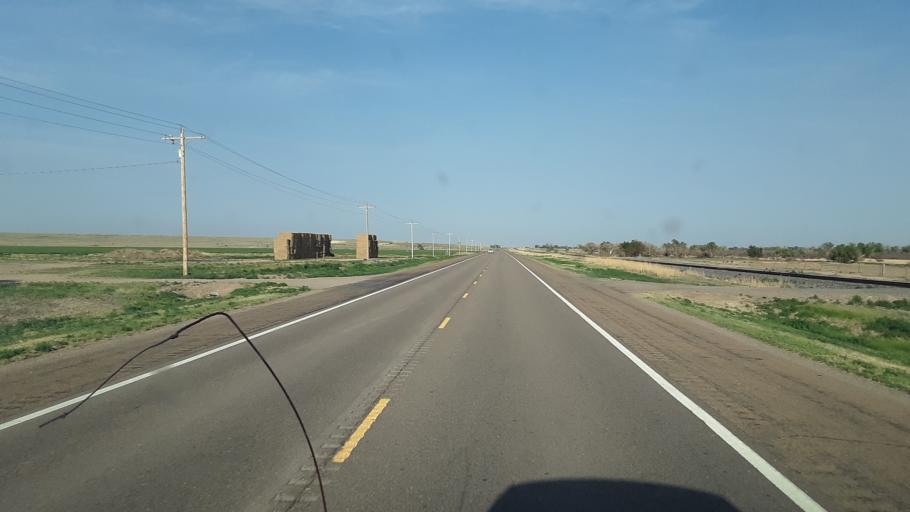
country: US
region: Kansas
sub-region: Hamilton County
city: Syracuse
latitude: 38.0267
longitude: -101.9365
